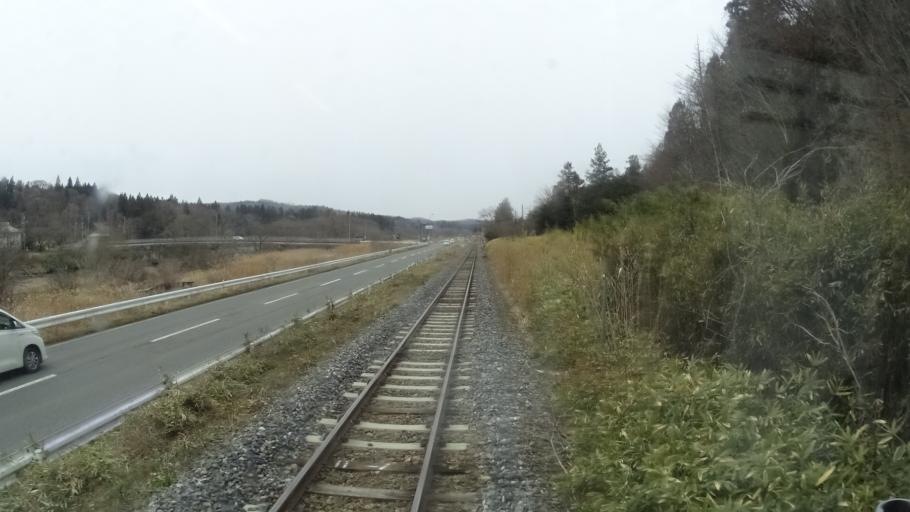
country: JP
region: Iwate
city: Hanamaki
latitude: 39.3618
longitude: 141.2798
